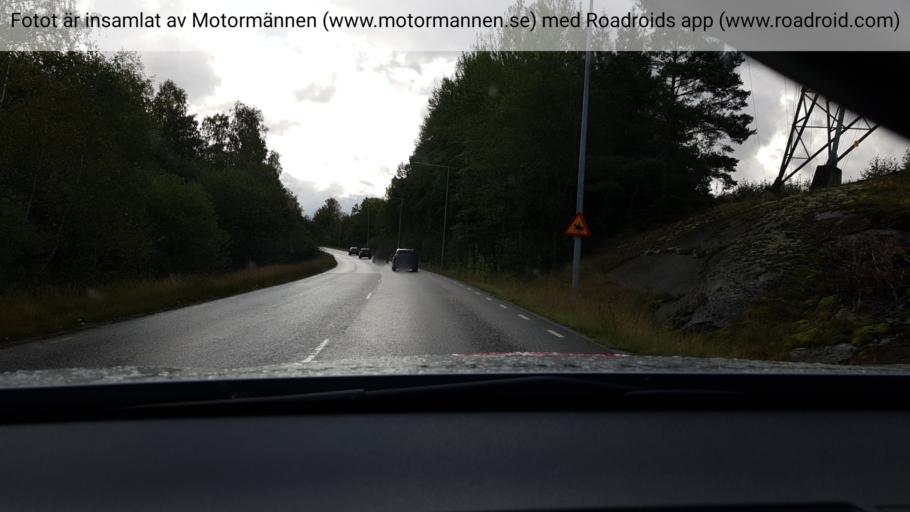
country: SE
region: Stockholm
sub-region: Stockholms Kommun
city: Arsta
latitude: 59.2285
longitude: 18.0544
